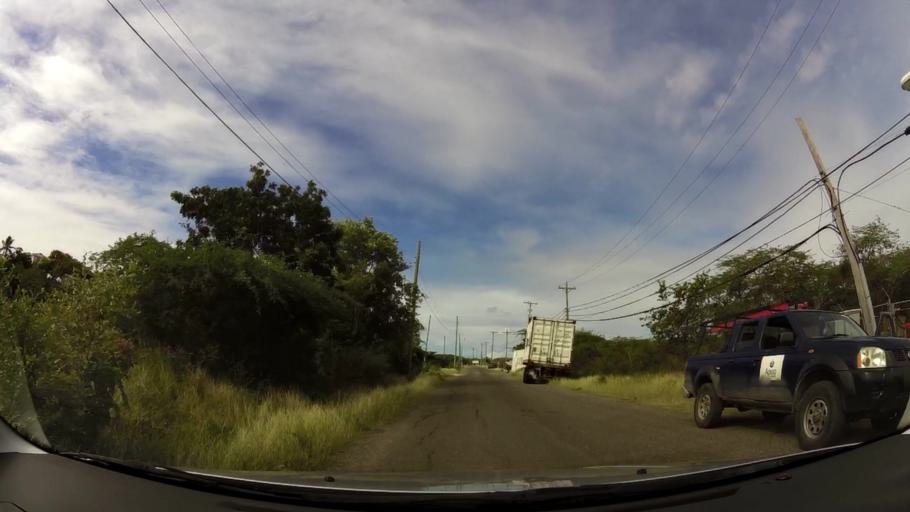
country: AG
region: Saint Paul
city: Falmouth
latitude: 17.0495
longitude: -61.7041
